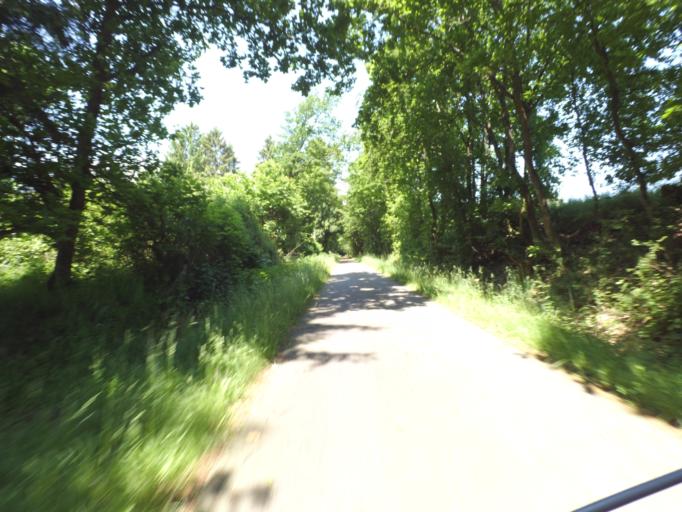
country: DE
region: Rheinland-Pfalz
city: Leiningen
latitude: 50.1241
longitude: 7.5677
